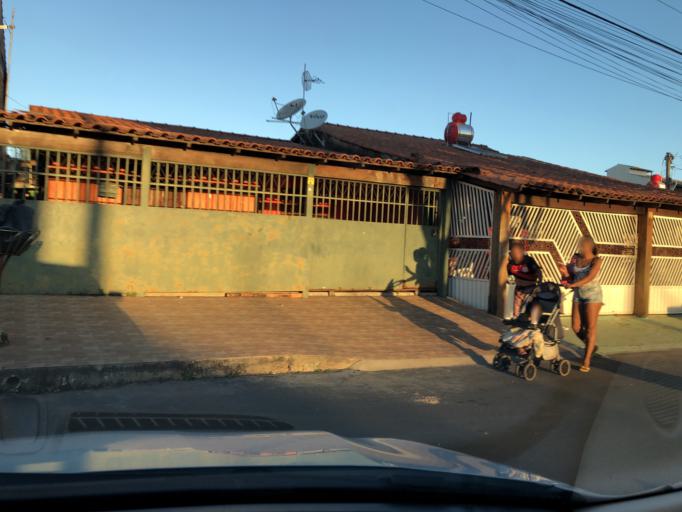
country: BR
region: Federal District
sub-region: Brasilia
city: Brasilia
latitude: -15.7734
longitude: -47.7820
